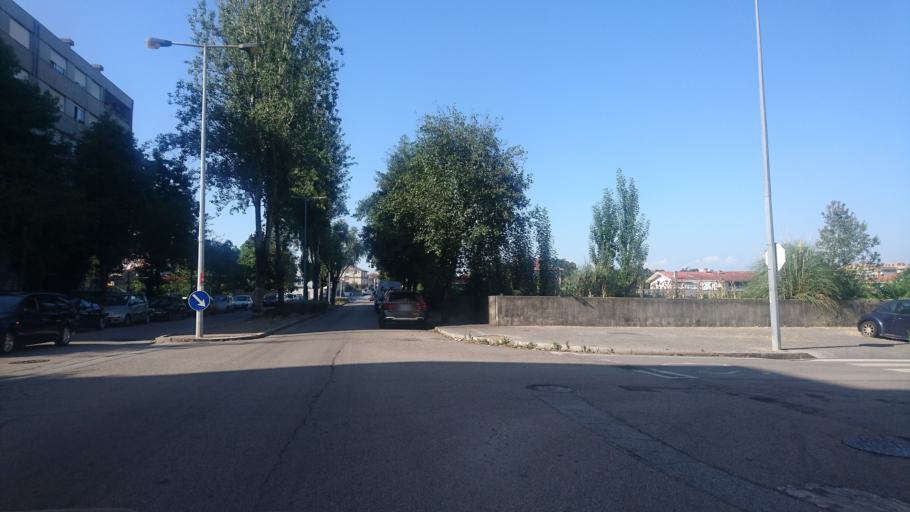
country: PT
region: Porto
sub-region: Valongo
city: Ermesinde
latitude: 41.2052
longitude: -8.5641
